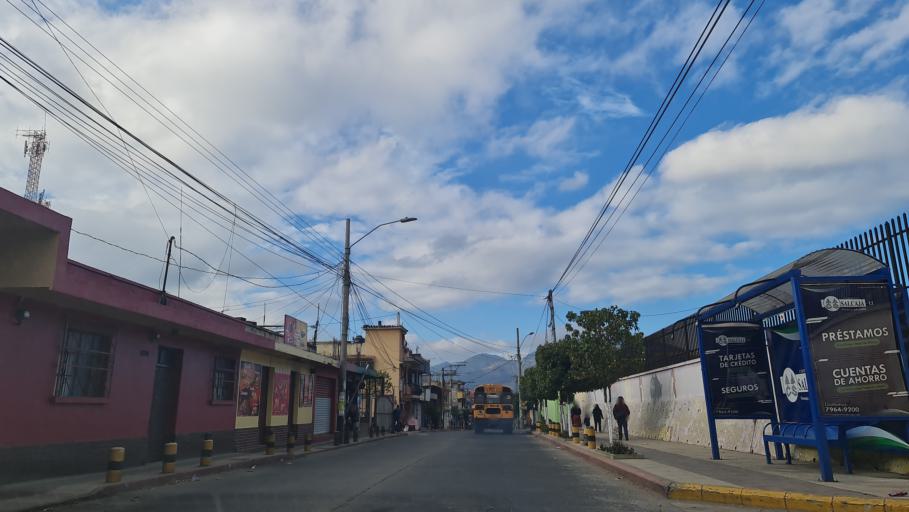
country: GT
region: San Marcos
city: San Pedro Sacatepequez
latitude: 14.9724
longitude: -91.7770
